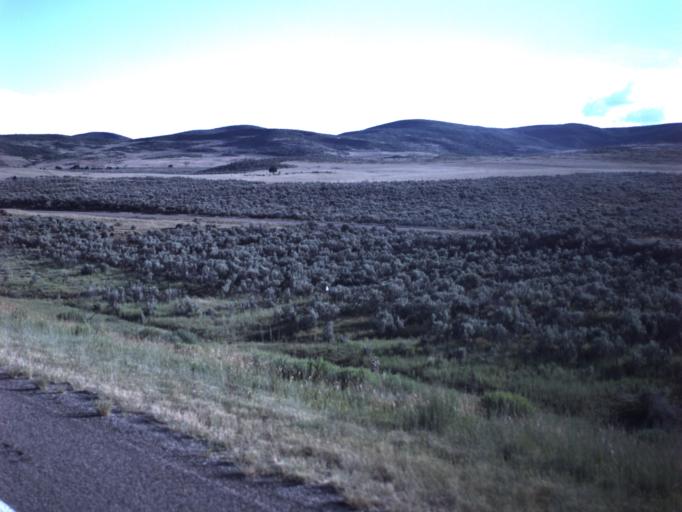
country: US
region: Utah
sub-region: Sanpete County
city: Fairview
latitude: 39.7134
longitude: -111.4715
